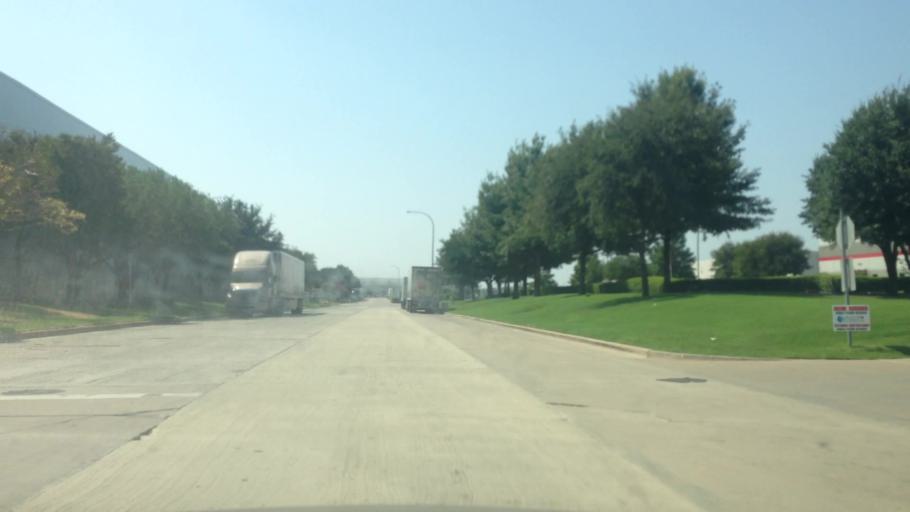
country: US
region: Texas
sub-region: Tarrant County
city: Blue Mound
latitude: 32.8320
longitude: -97.3524
